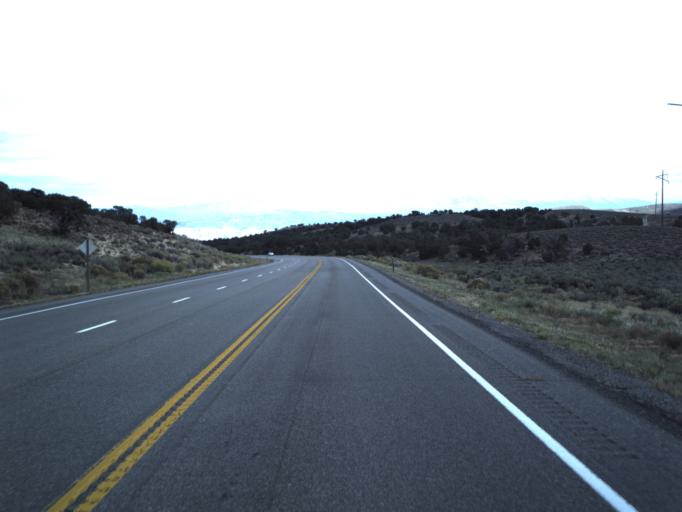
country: US
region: Utah
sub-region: Sevier County
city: Aurora
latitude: 38.9935
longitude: -112.0093
